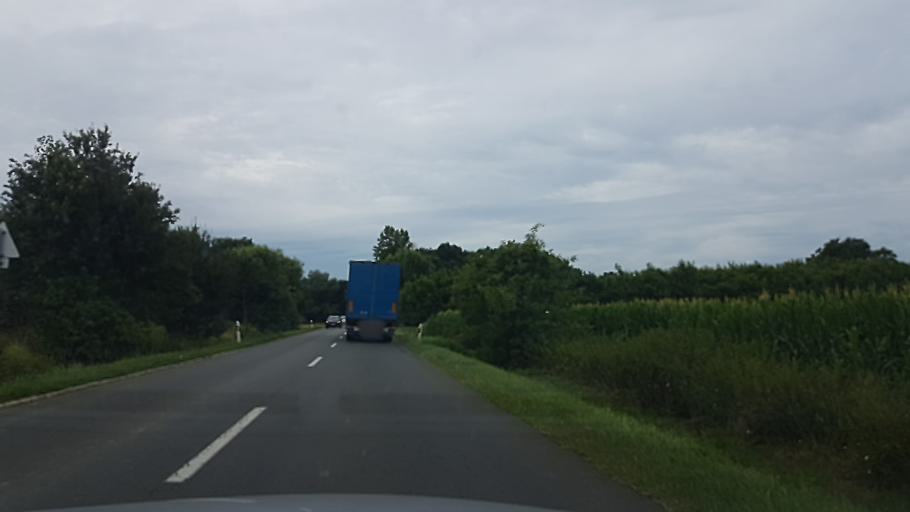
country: HU
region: Baranya
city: Szigetvar
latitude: 46.0347
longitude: 17.6830
